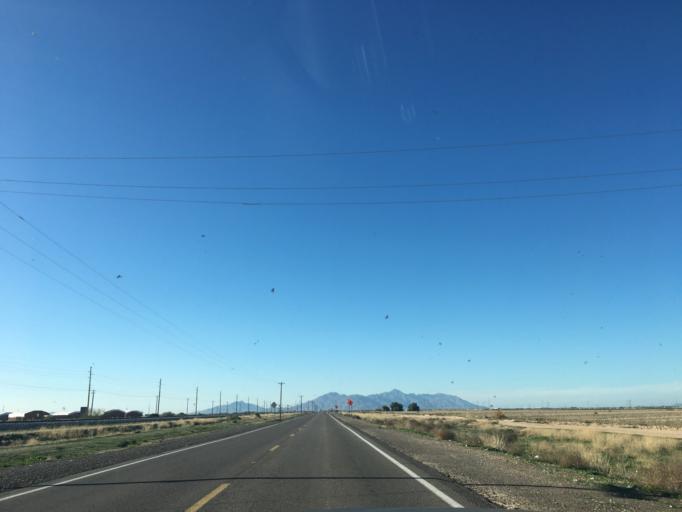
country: US
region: Arizona
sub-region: Pinal County
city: Maricopa
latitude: 33.0155
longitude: -111.9811
